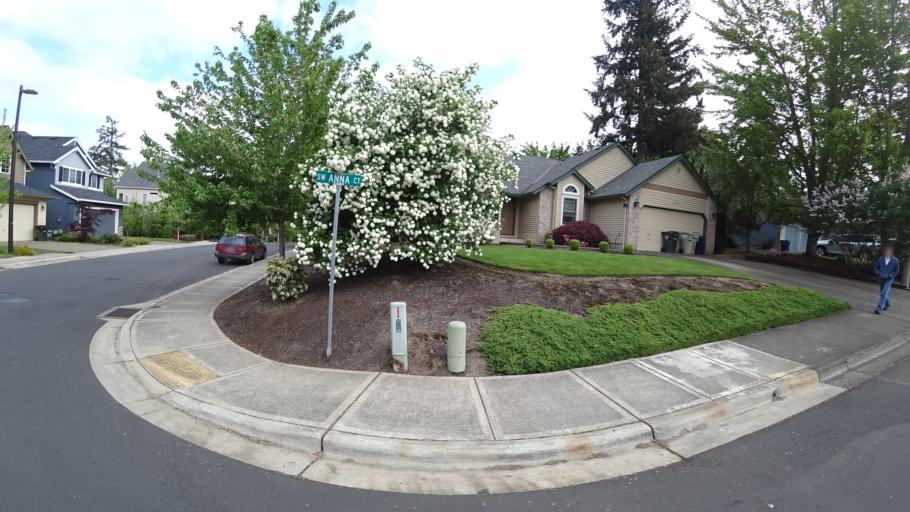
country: US
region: Oregon
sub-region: Washington County
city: Aloha
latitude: 45.5175
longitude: -122.8910
